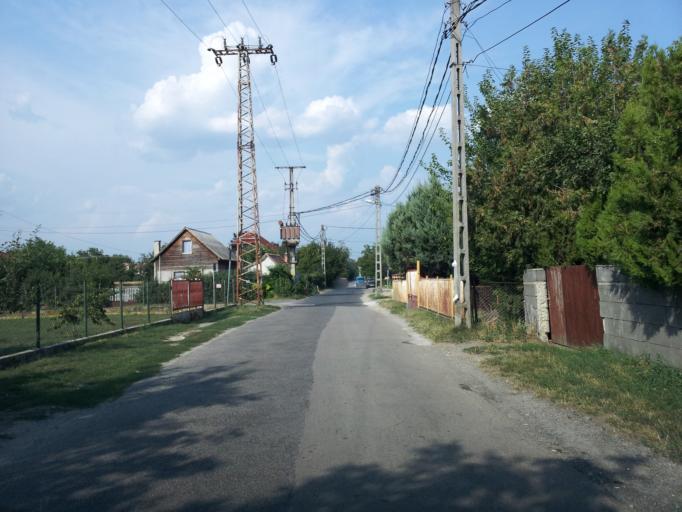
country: HU
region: Pest
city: Szigethalom
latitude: 47.3086
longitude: 19.0163
